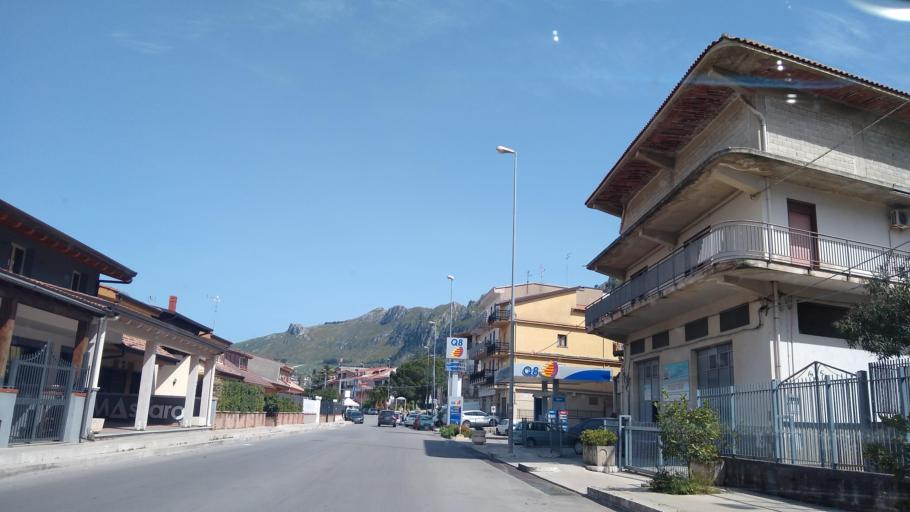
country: IT
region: Sicily
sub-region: Palermo
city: San Giuseppe Jato
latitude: 37.9753
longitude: 13.1923
